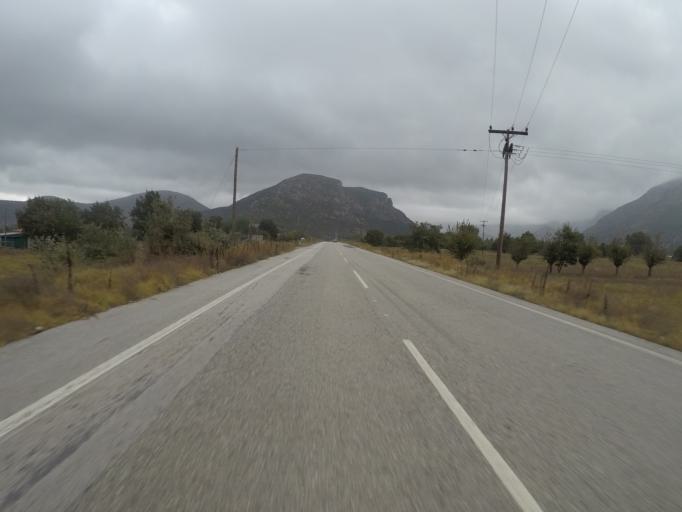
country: GR
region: Peloponnese
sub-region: Nomos Arkadias
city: Tripoli
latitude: 37.5877
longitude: 22.4263
